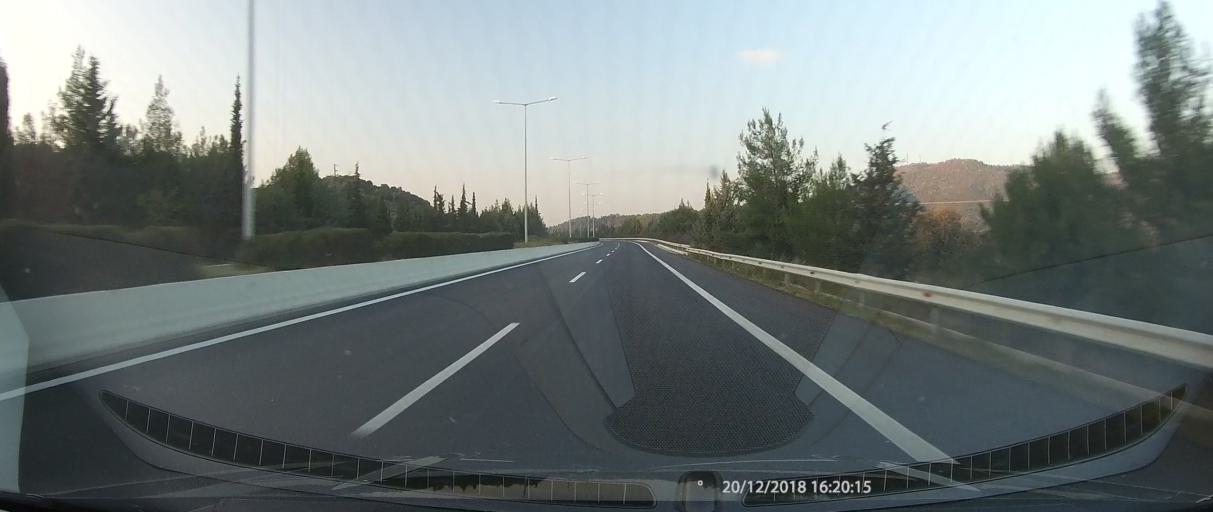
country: GR
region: Thessaly
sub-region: Nomos Magnisias
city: Pteleos
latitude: 39.0260
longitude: 22.9124
